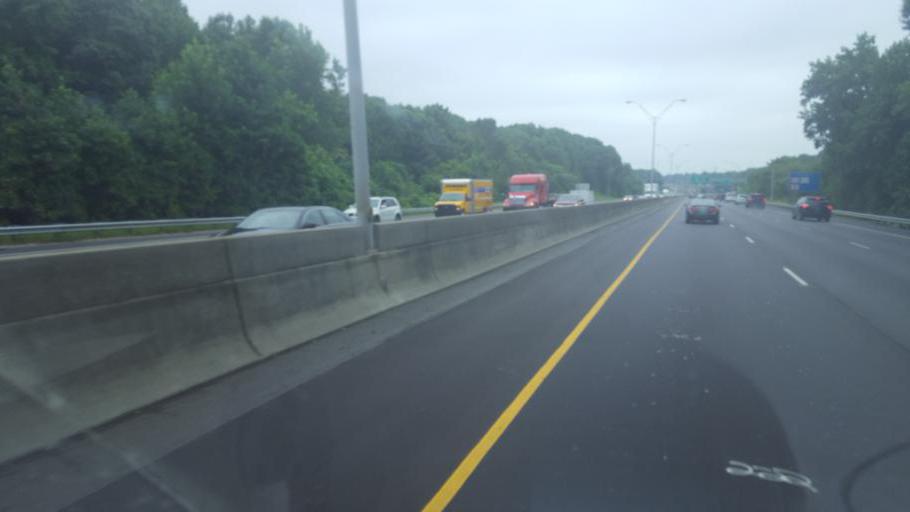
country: US
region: North Carolina
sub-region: Mecklenburg County
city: Pineville
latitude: 35.1554
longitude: -80.8926
